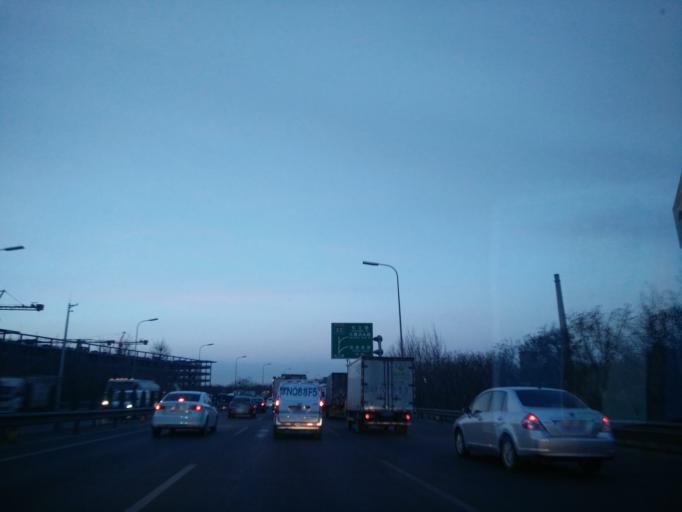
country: CN
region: Beijing
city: Dongfeng
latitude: 39.8523
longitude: 116.5436
